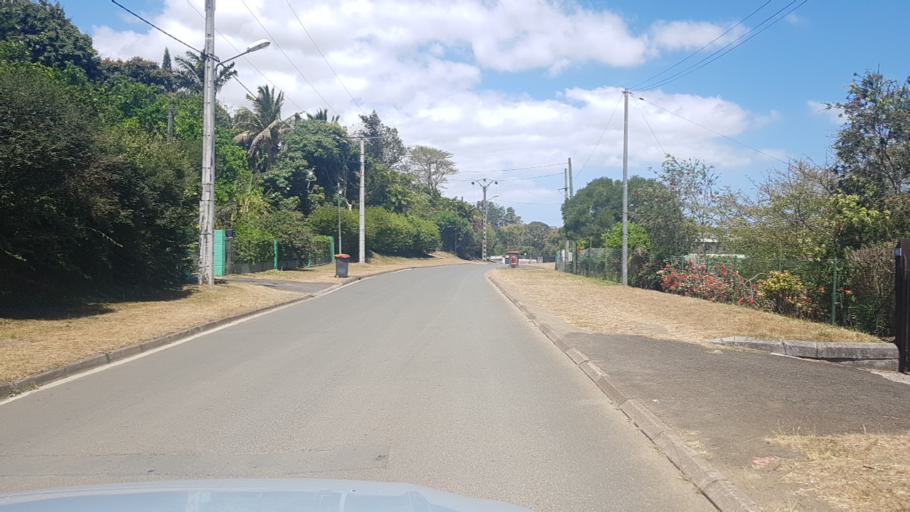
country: NC
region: South Province
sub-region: Dumbea
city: Dumbea
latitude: -22.1330
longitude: 166.4309
